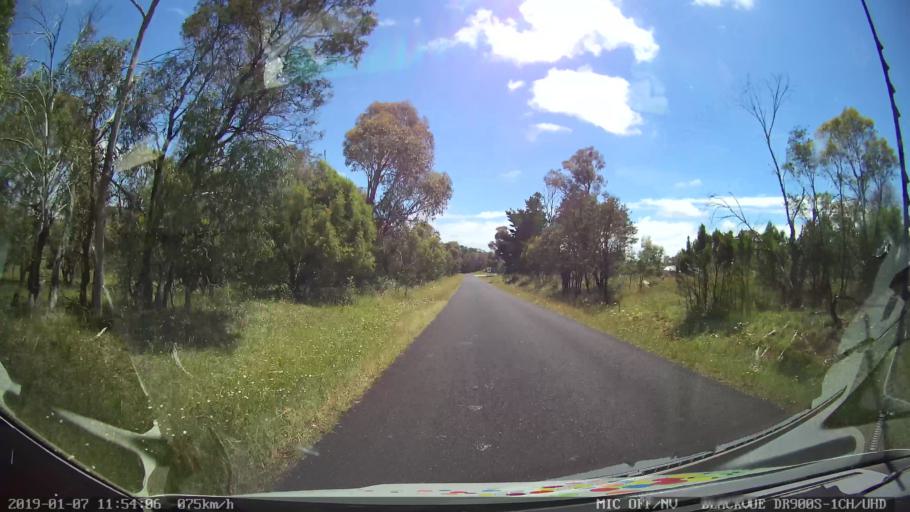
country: AU
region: New South Wales
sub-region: Guyra
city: Guyra
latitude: -30.2998
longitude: 151.6637
